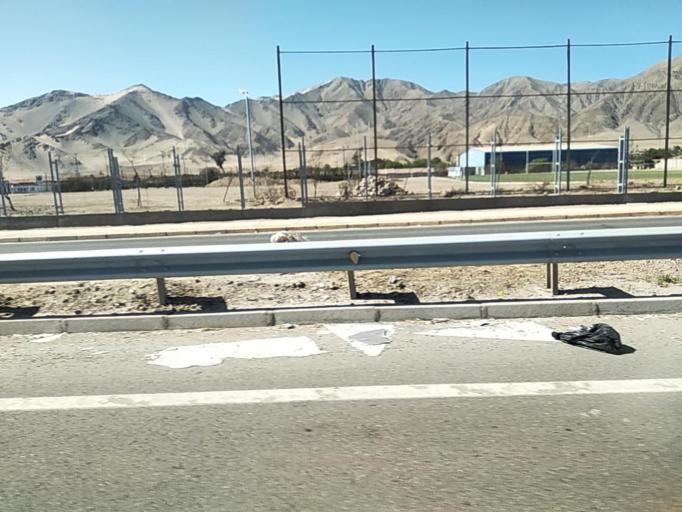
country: CL
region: Atacama
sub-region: Provincia de Copiapo
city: Copiapo
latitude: -27.3493
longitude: -70.3540
